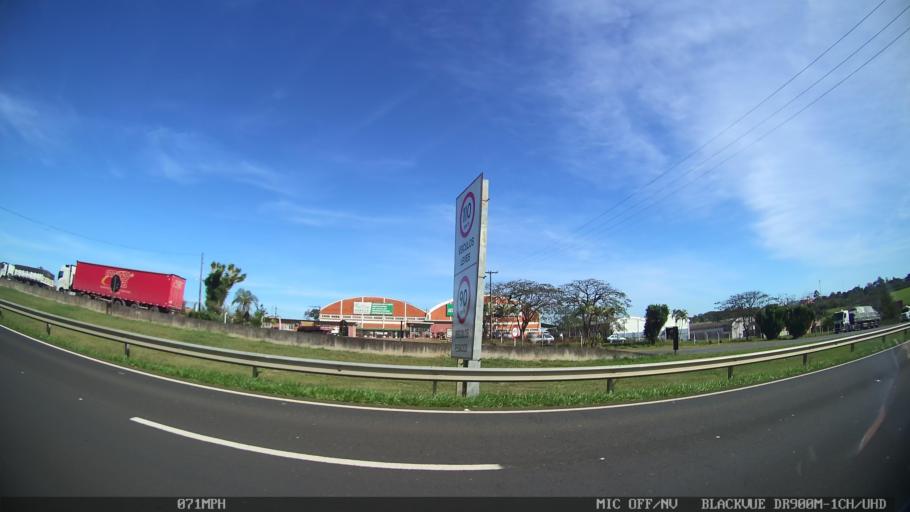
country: BR
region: Sao Paulo
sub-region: Araras
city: Araras
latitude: -22.3830
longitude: -47.3942
